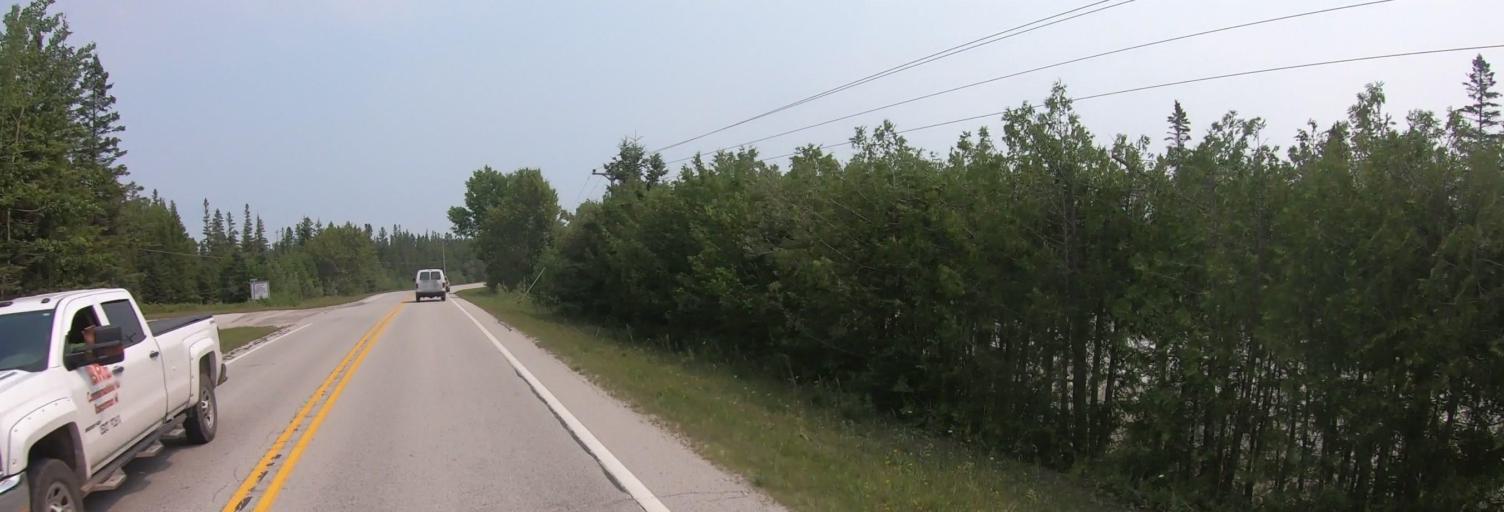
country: CA
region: Ontario
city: Thessalon
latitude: 45.9963
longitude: -83.8586
